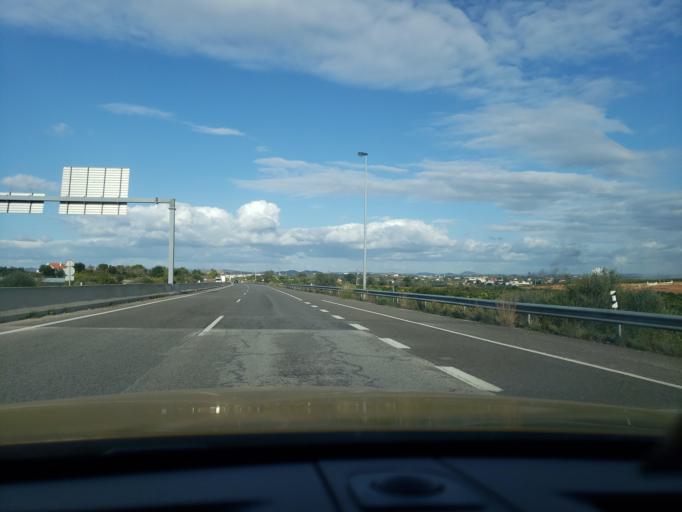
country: PT
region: Faro
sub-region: Lagoa
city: Lagoa
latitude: 37.1618
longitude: -8.4456
